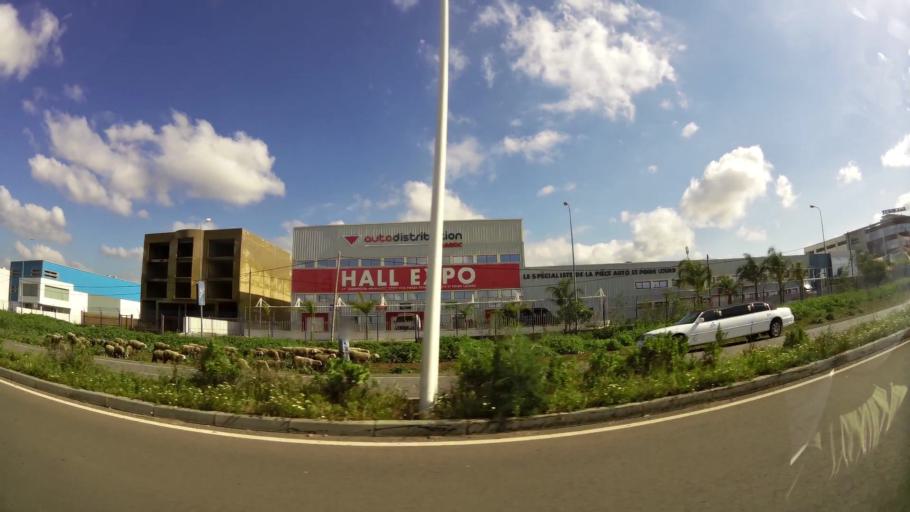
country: MA
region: Grand Casablanca
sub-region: Mediouna
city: Mediouna
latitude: 33.4061
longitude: -7.5518
